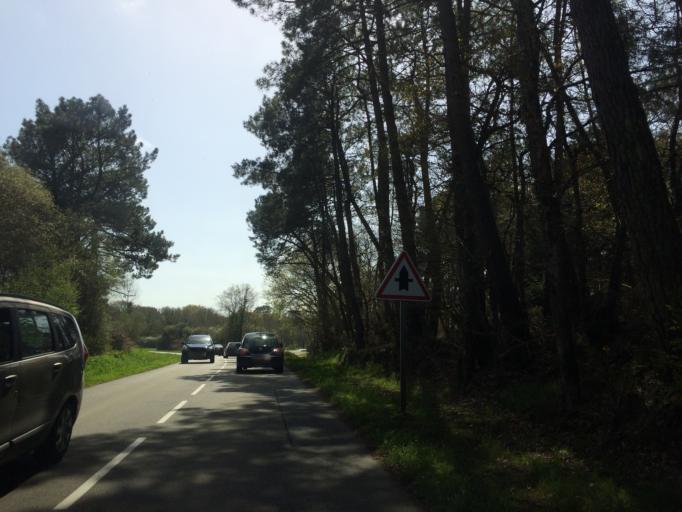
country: FR
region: Brittany
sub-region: Departement du Morbihan
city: Ploemel
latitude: 47.6192
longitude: -3.0549
